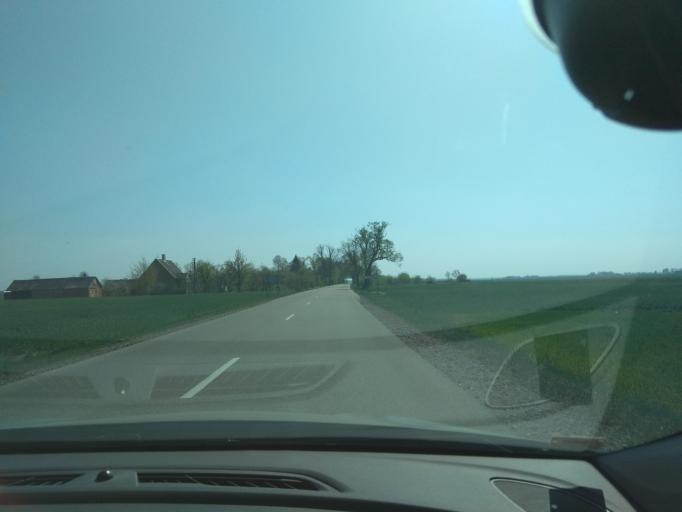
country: LT
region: Panevezys
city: Pasvalys
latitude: 55.9502
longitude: 24.2128
